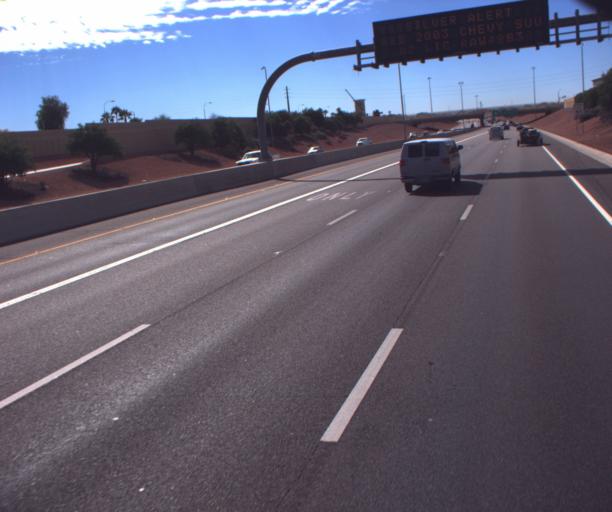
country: US
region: Arizona
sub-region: Maricopa County
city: San Carlos
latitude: 33.3236
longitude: -111.8939
